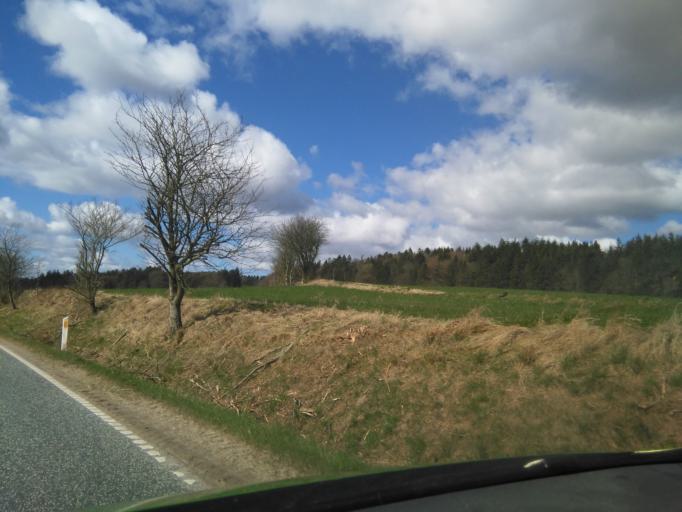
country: DK
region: Central Jutland
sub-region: Horsens Kommune
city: Braedstrup
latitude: 56.0259
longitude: 9.5595
